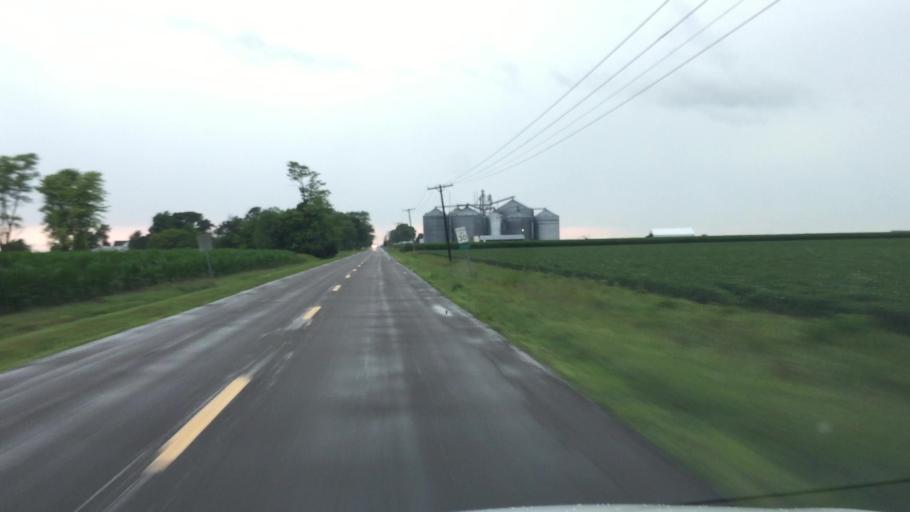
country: US
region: Illinois
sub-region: Hancock County
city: Carthage
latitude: 40.5207
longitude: -91.1599
